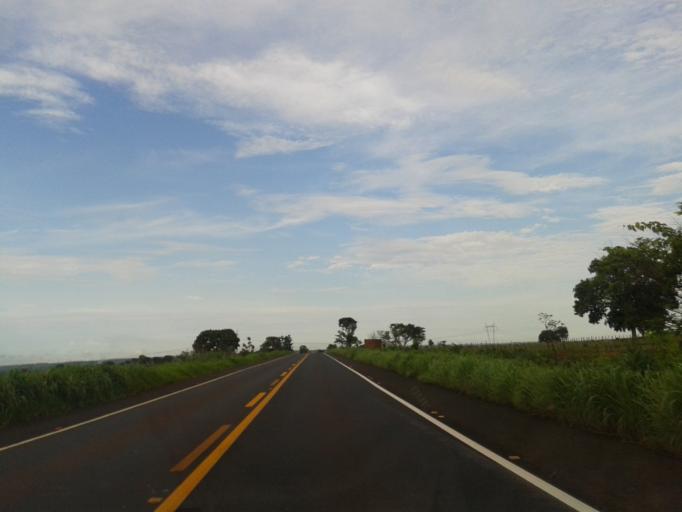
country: BR
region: Minas Gerais
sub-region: Santa Vitoria
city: Santa Vitoria
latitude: -19.0461
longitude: -50.4696
